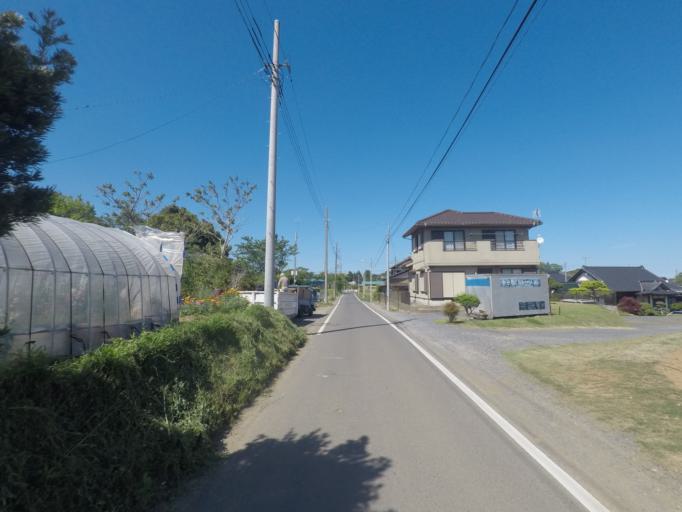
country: JP
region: Ibaraki
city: Itako
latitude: 36.0293
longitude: 140.4726
